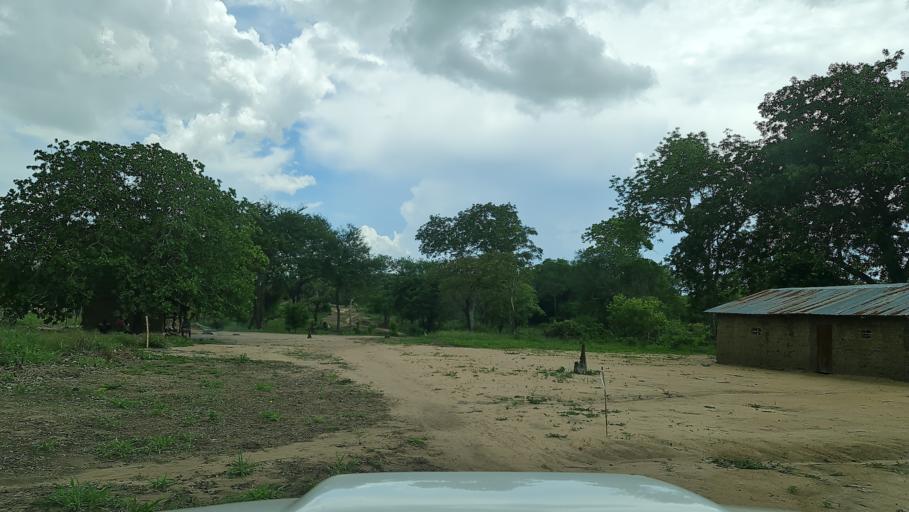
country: MZ
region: Nampula
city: Ilha de Mocambique
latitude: -15.5000
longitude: 40.1589
